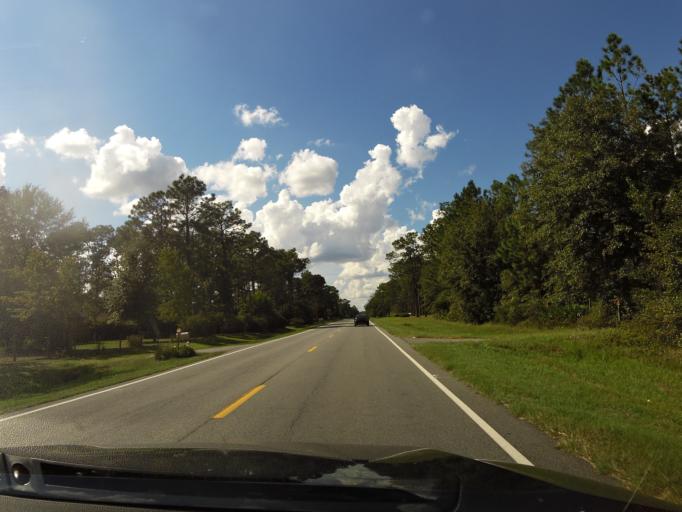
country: US
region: Georgia
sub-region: Lowndes County
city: Valdosta
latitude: 30.7972
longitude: -83.1909
